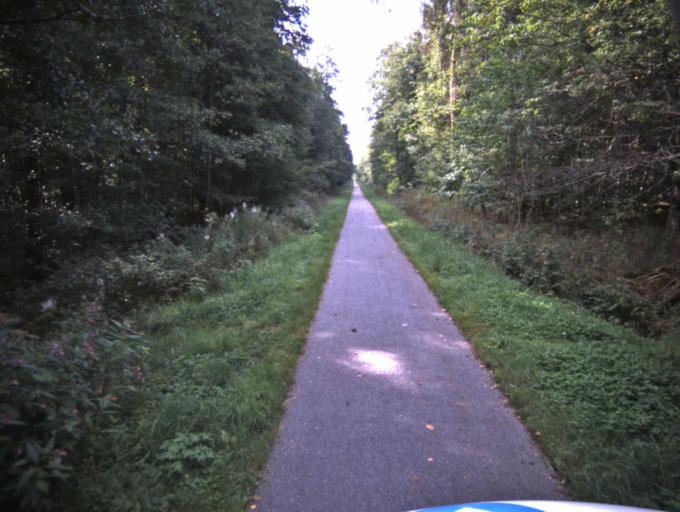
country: SE
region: Vaestra Goetaland
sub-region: Ulricehamns Kommun
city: Ulricehamn
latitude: 57.6672
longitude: 13.3667
